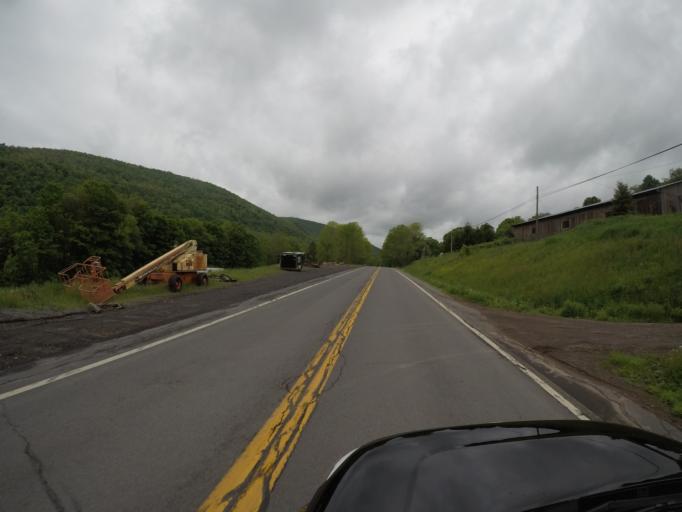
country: US
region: New York
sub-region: Delaware County
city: Delhi
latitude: 42.2499
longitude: -74.8351
